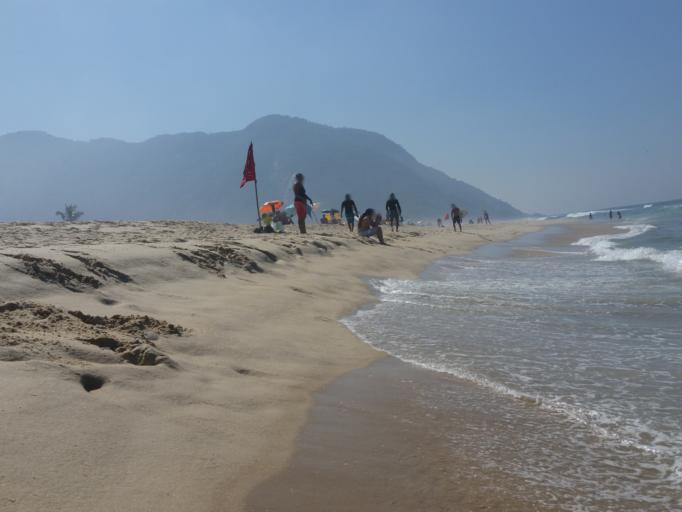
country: BR
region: Rio de Janeiro
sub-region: Nilopolis
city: Nilopolis
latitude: -23.0496
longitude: -43.5302
